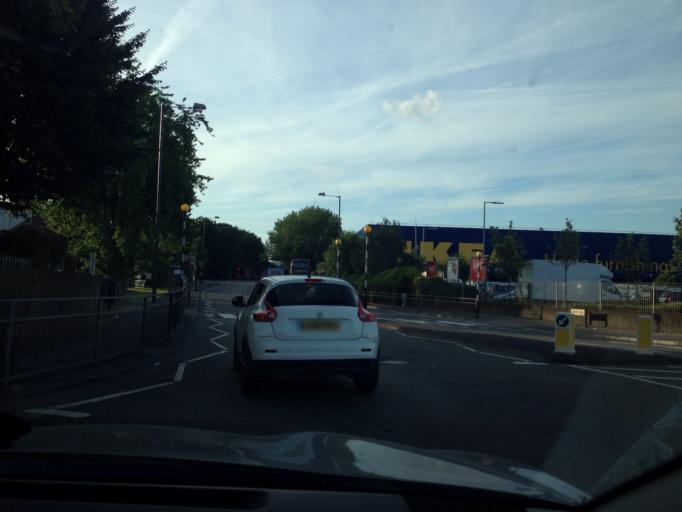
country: GB
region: England
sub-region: Greater London
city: Wembley
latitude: 51.5526
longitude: -0.2616
